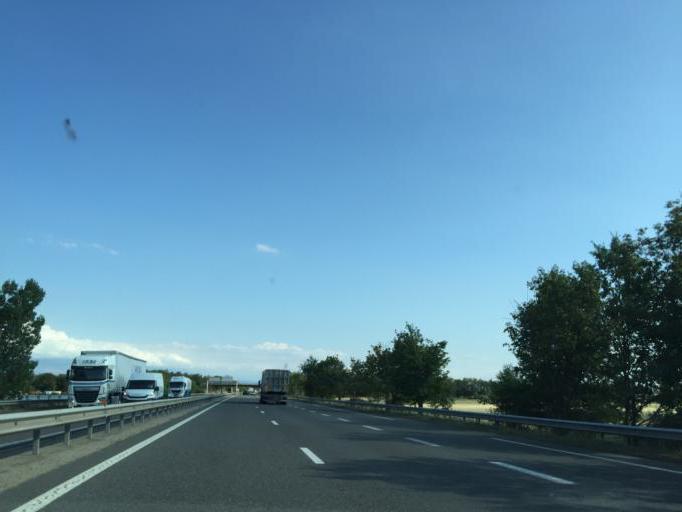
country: FR
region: Rhone-Alpes
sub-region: Departement de la Loire
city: Montrond-les-Bains
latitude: 45.6379
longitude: 4.1912
